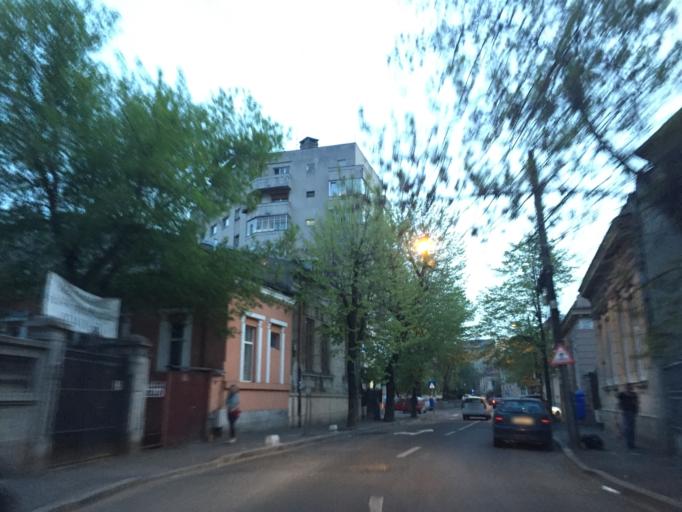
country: RO
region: Bucuresti
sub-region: Municipiul Bucuresti
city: Bucharest
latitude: 44.4363
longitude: 26.1139
